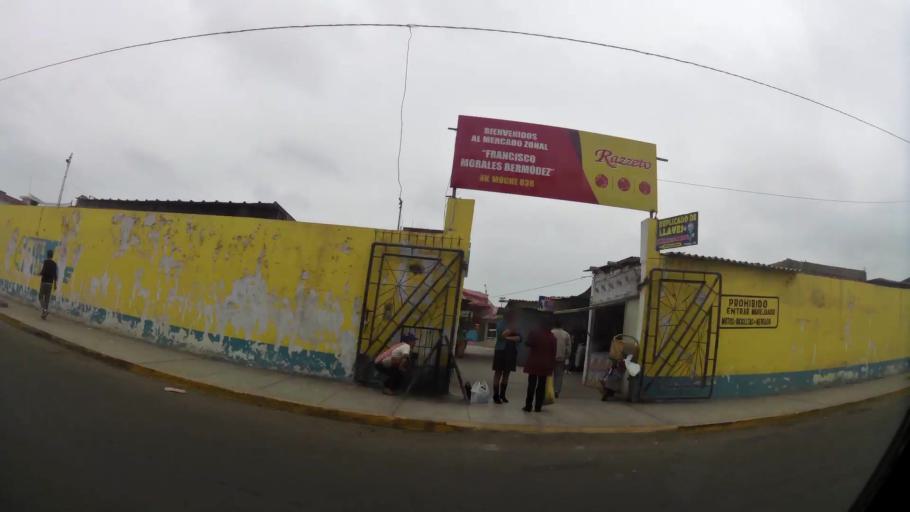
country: PE
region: La Libertad
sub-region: Provincia de Trujillo
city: Trujillo
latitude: -8.1222
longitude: -79.0236
